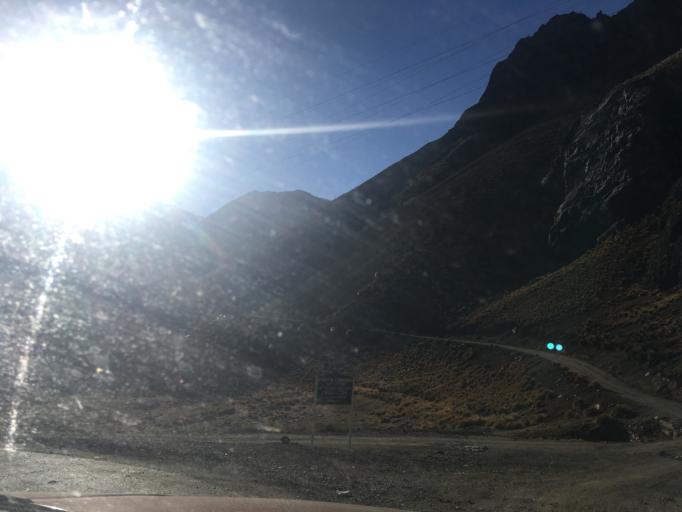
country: BO
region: La Paz
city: Quime
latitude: -17.0482
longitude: -67.2951
